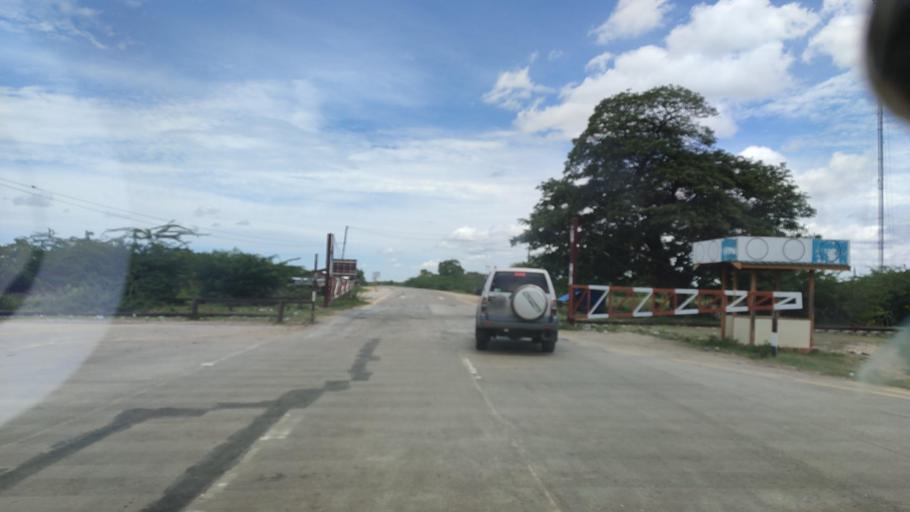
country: MM
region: Mandalay
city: Meiktila
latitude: 20.8579
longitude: 95.9576
